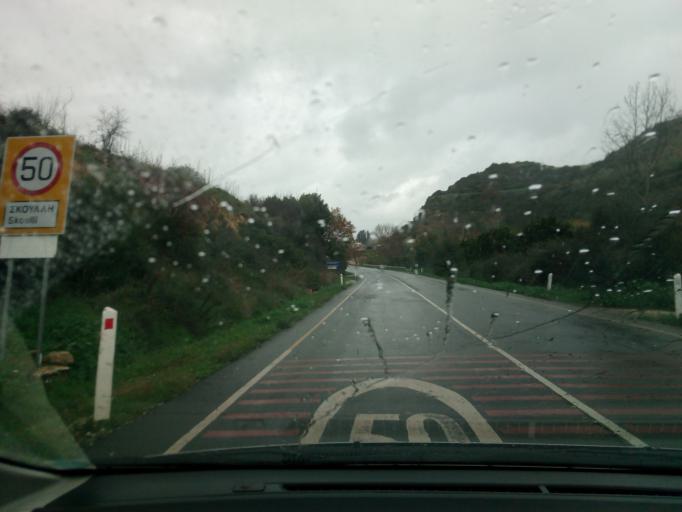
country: CY
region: Pafos
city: Polis
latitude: 34.9756
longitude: 32.4505
